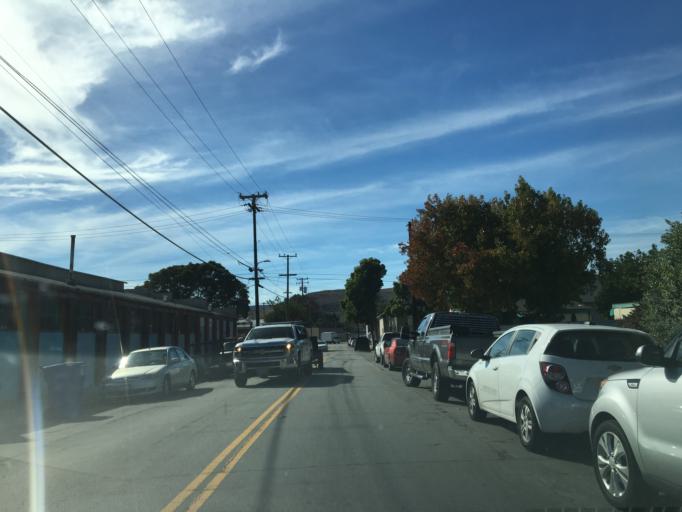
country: US
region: California
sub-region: San Luis Obispo County
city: San Luis Obispo
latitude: 35.2746
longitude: -120.6679
